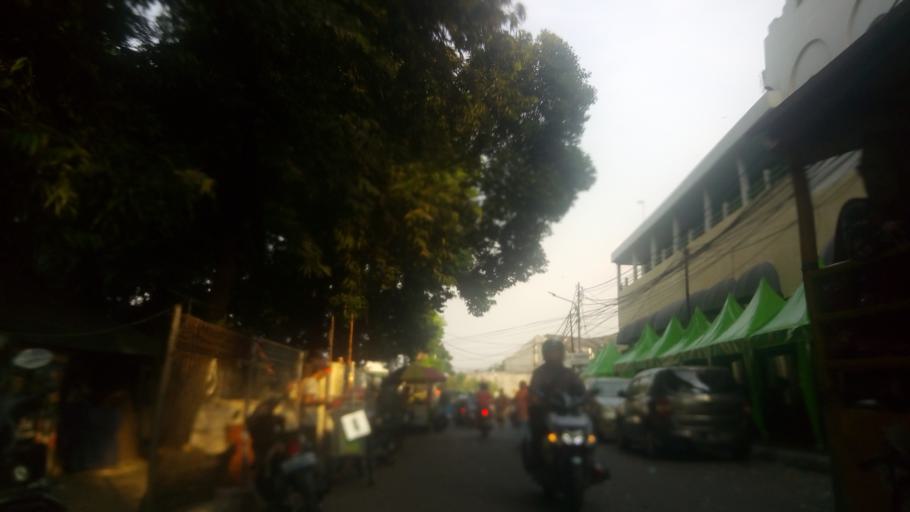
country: ID
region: Jakarta Raya
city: Jakarta
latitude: -6.2024
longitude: 106.8512
